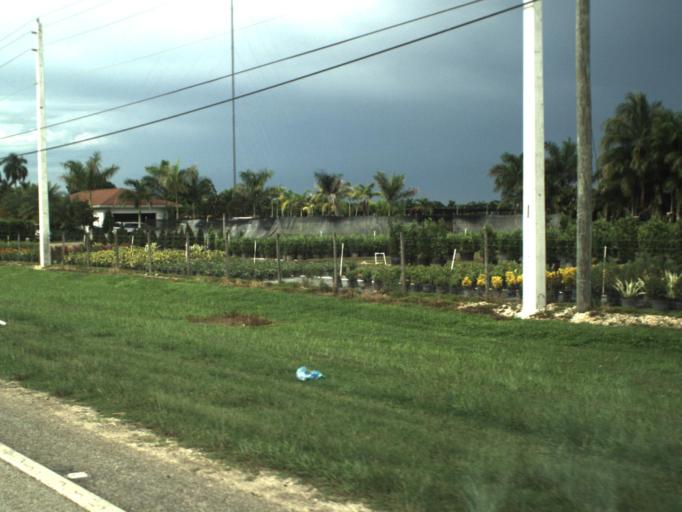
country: US
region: Florida
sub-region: Miami-Dade County
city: Naranja
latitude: 25.5256
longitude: -80.4779
